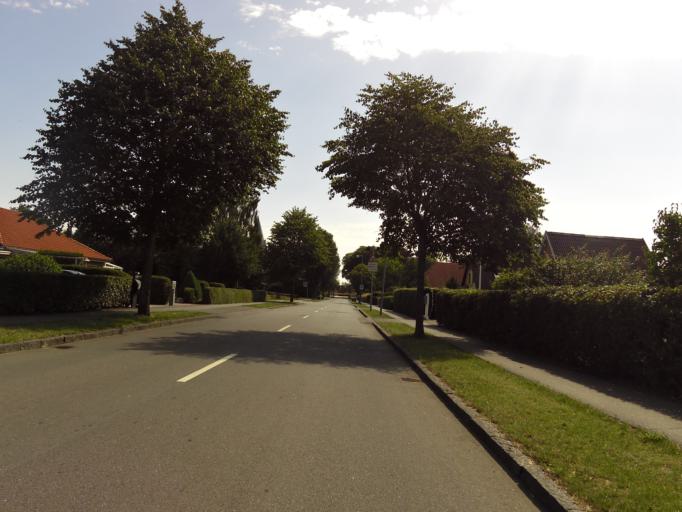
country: DK
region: South Denmark
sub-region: Haderslev Kommune
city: Vojens
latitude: 55.1990
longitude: 9.2011
